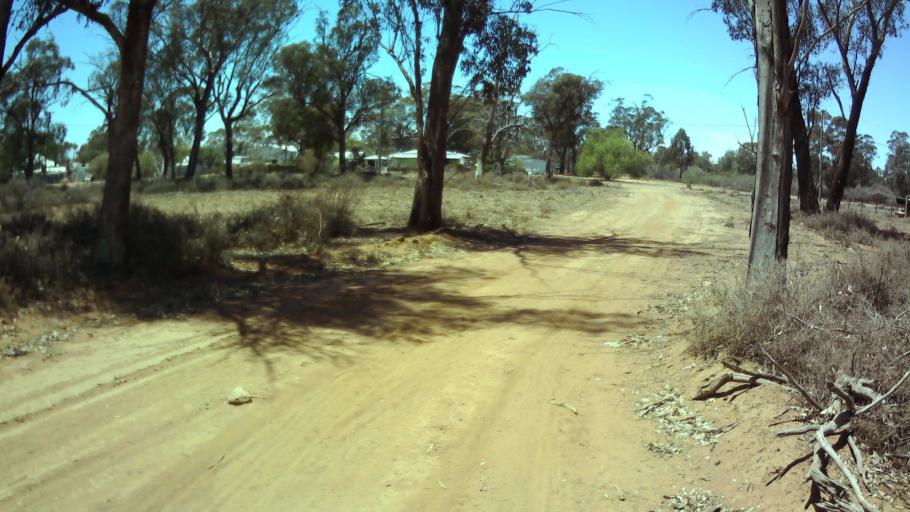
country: AU
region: New South Wales
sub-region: Weddin
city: Grenfell
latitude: -33.8449
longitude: 147.7379
